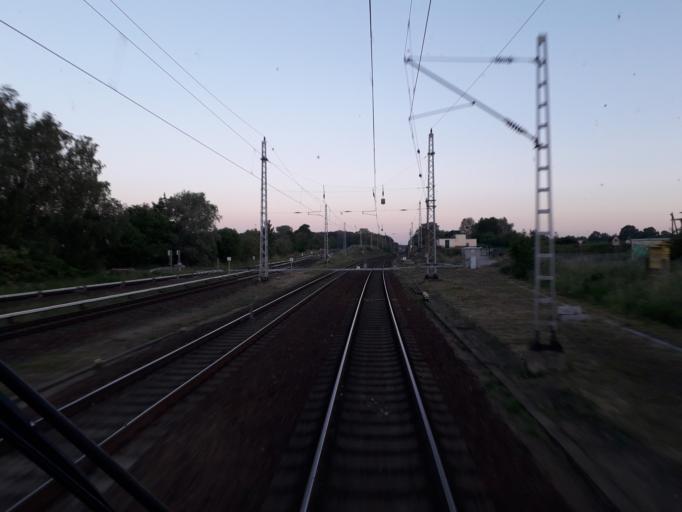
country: DE
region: Brandenburg
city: Glienicke
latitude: 52.6658
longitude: 13.3362
